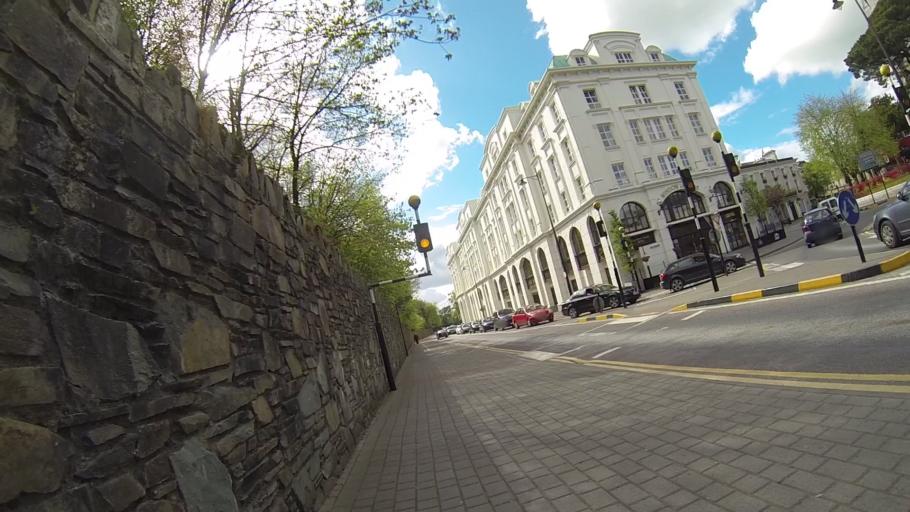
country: IE
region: Munster
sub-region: Ciarrai
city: Cill Airne
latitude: 52.0575
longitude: -9.5080
